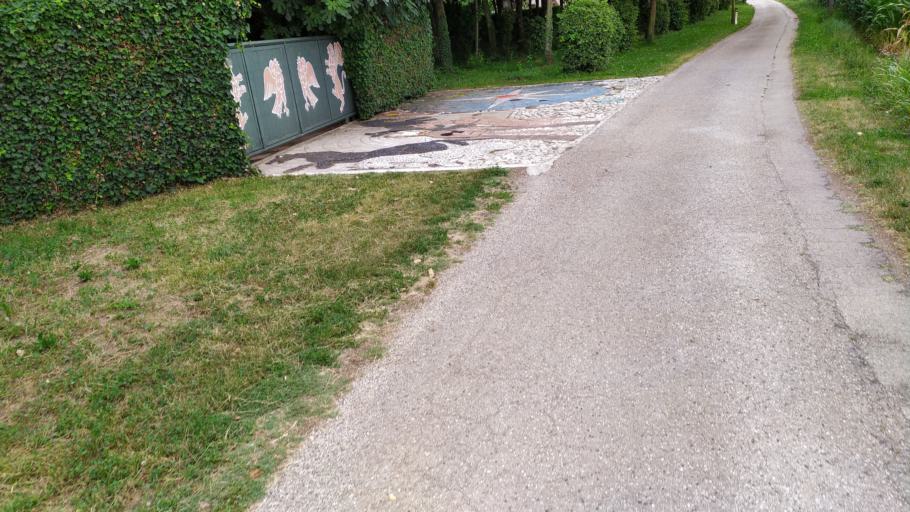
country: IT
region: Veneto
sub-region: Provincia di Vicenza
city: Villaverla
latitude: 45.6484
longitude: 11.4690
